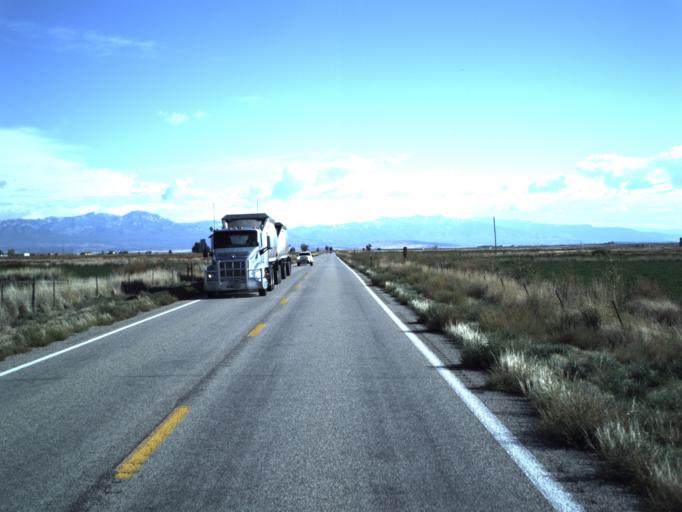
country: US
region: Utah
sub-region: Millard County
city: Delta
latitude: 39.2159
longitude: -112.4177
